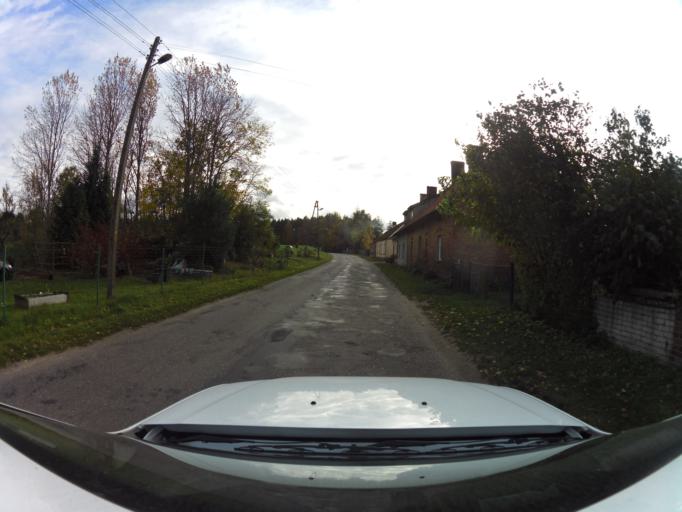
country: PL
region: West Pomeranian Voivodeship
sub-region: Powiat gryficki
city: Gryfice
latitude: 53.8657
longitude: 15.1147
